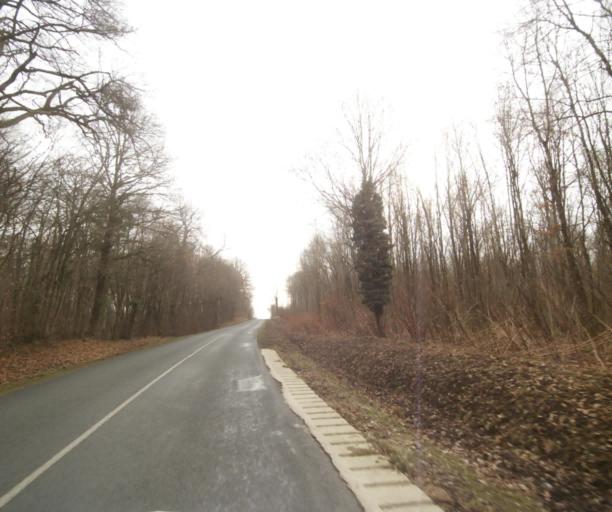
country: FR
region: Champagne-Ardenne
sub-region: Departement de la Haute-Marne
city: Villiers-en-Lieu
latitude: 48.7080
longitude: 4.8909
